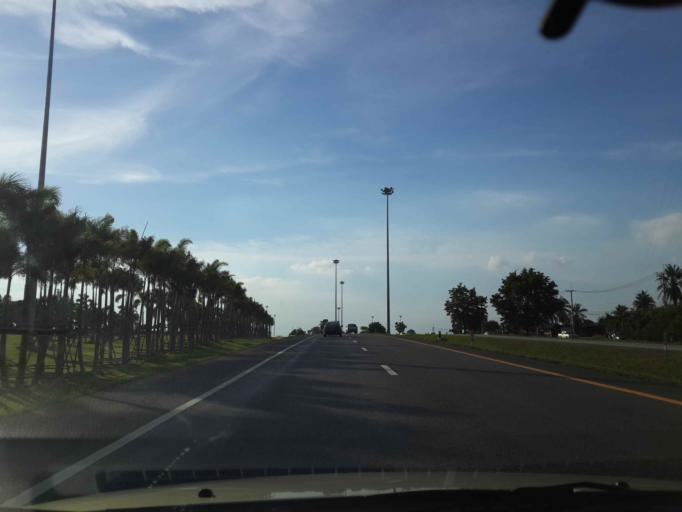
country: TH
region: Chon Buri
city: Bang Lamung
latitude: 12.9624
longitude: 100.9823
